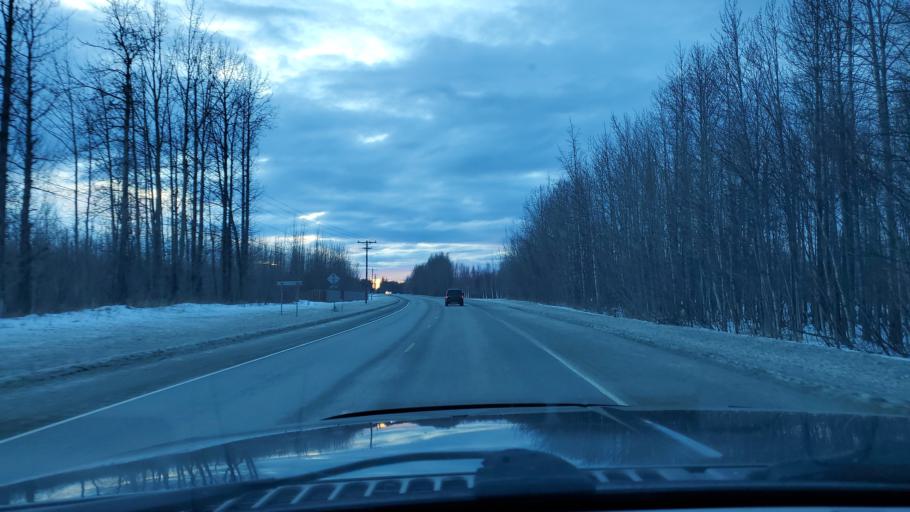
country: US
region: Alaska
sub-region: Matanuska-Susitna Borough
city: Farm Loop
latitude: 61.6630
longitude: -149.0886
